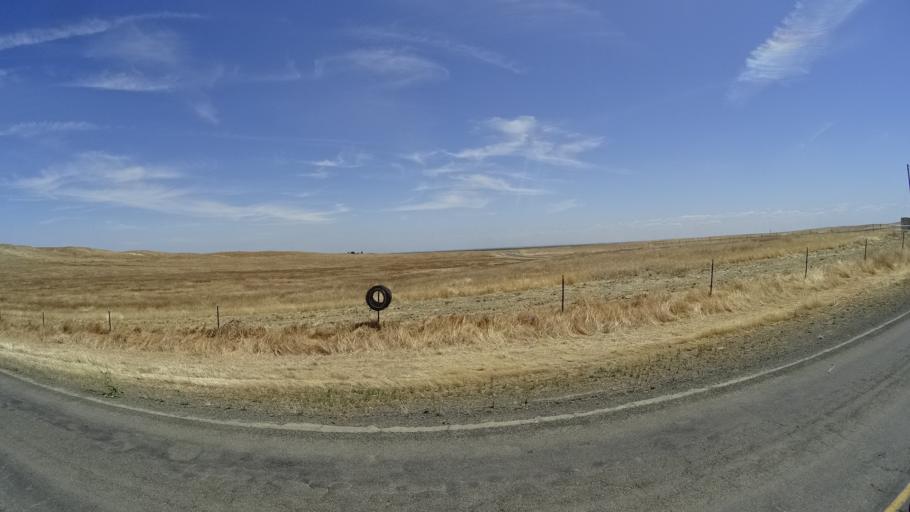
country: US
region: California
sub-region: Kings County
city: Kettleman City
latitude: 35.8588
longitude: -119.9153
